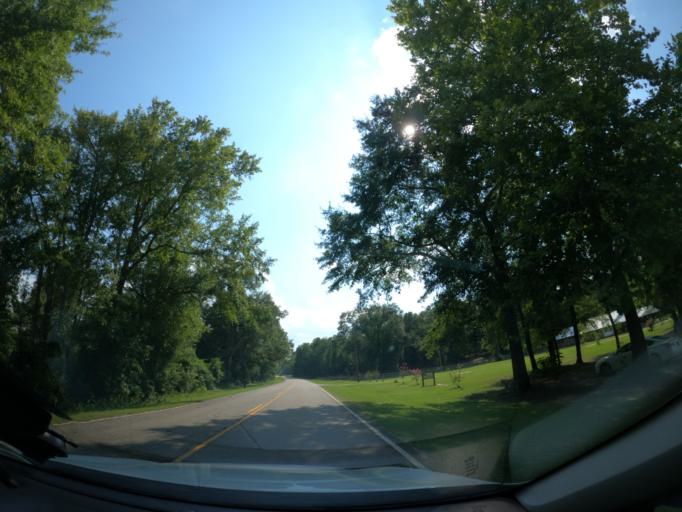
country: US
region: South Carolina
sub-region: Barnwell County
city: Williston
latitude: 33.5913
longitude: -81.4647
